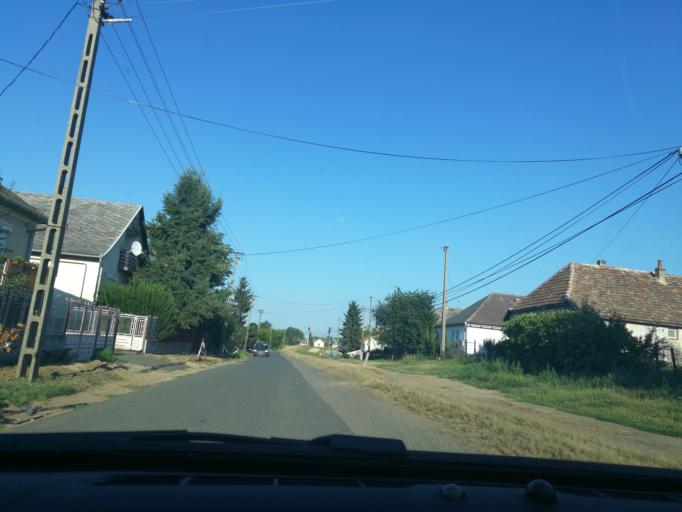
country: HU
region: Szabolcs-Szatmar-Bereg
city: Tiszabercel
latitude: 48.1690
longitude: 21.5710
